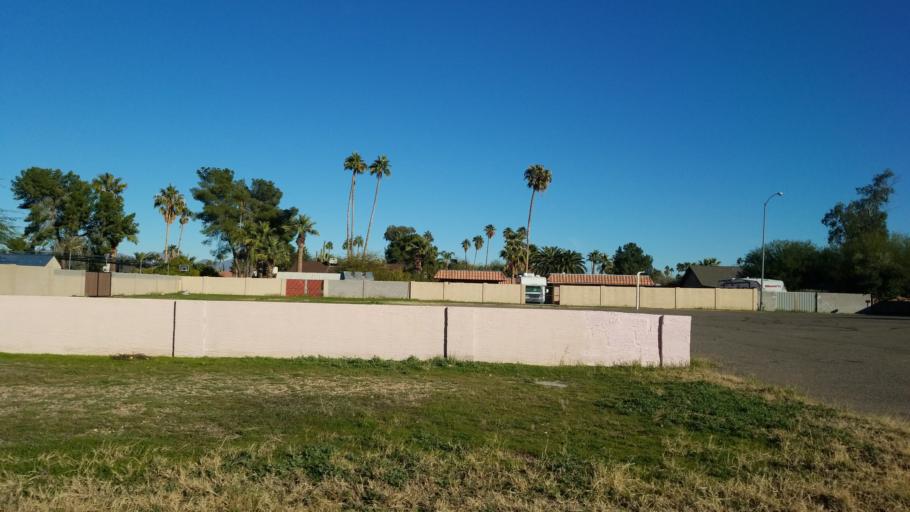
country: US
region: Arizona
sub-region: Maricopa County
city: Paradise Valley
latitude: 33.5876
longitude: -112.0074
